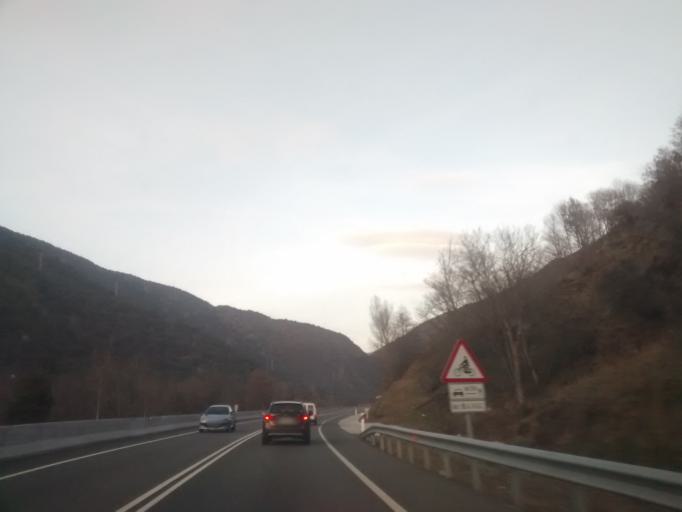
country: ES
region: Catalonia
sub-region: Provincia de Lleida
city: la Seu d'Urgell
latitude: 42.3854
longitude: 1.4600
